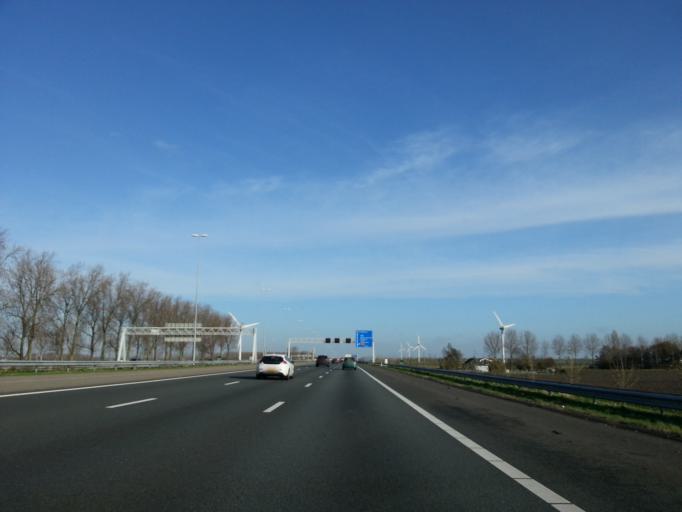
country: NL
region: South Holland
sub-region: Gemeente Kaag en Braassem
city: Oude Wetering
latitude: 52.2239
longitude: 4.6353
